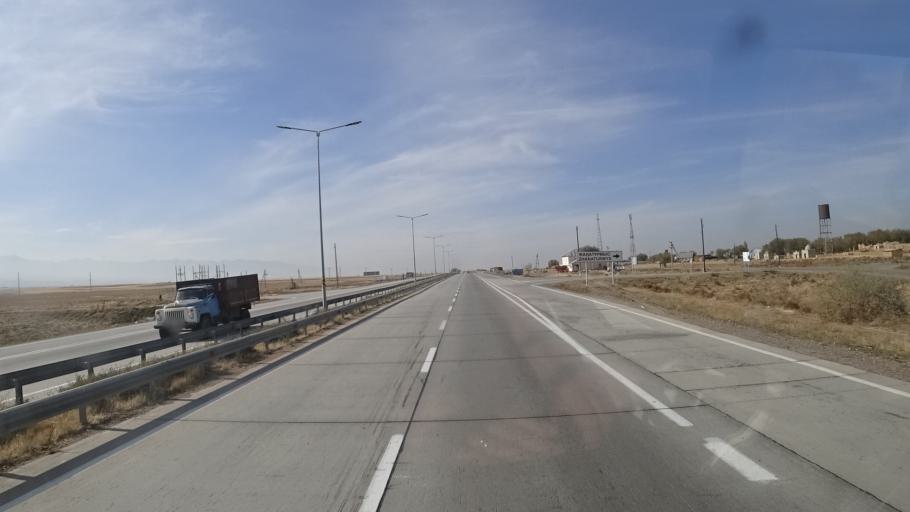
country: KZ
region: Zhambyl
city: Merke
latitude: 42.8891
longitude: 72.9889
